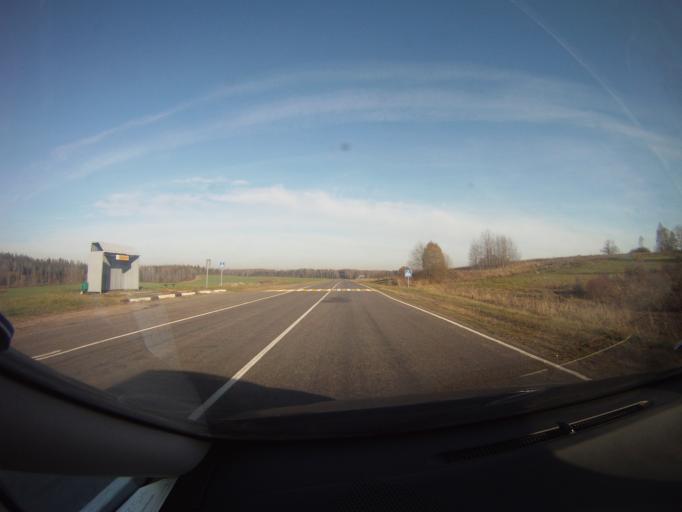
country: BY
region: Minsk
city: Il'ya
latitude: 54.2622
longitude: 27.4942
